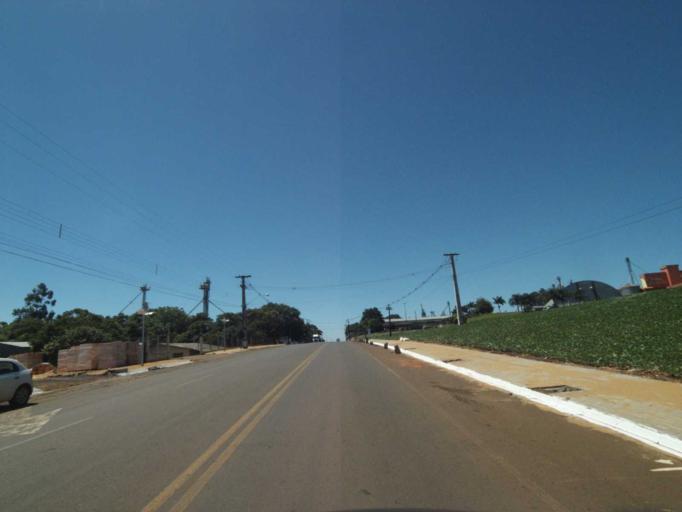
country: BR
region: Parana
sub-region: Coronel Vivida
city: Coronel Vivida
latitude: -25.9768
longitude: -52.8133
